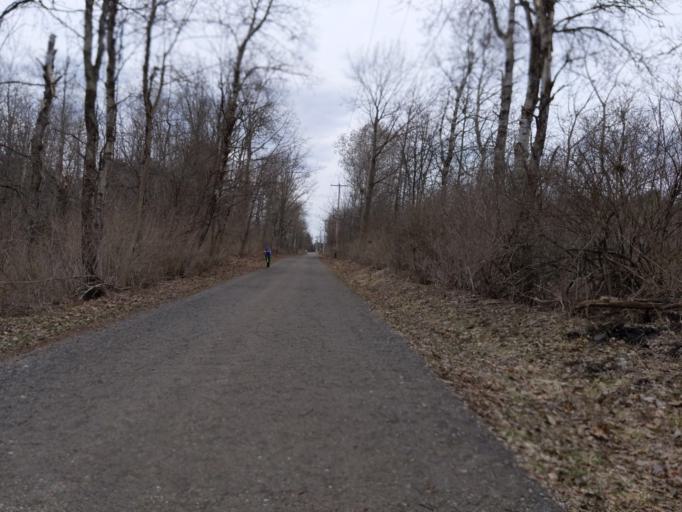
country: US
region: New York
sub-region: Tompkins County
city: Dryden
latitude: 42.5090
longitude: -76.3432
